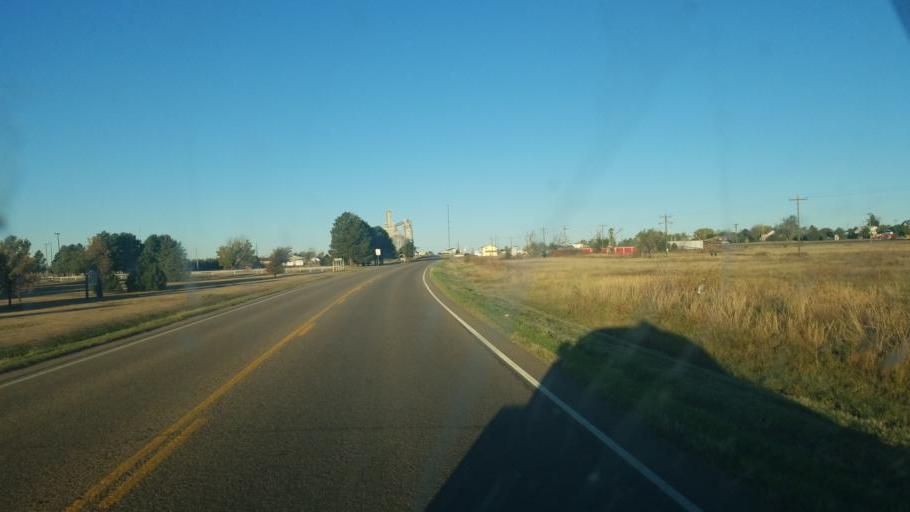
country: US
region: Colorado
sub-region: Cheyenne County
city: Cheyenne Wells
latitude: 38.8164
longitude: -102.3513
